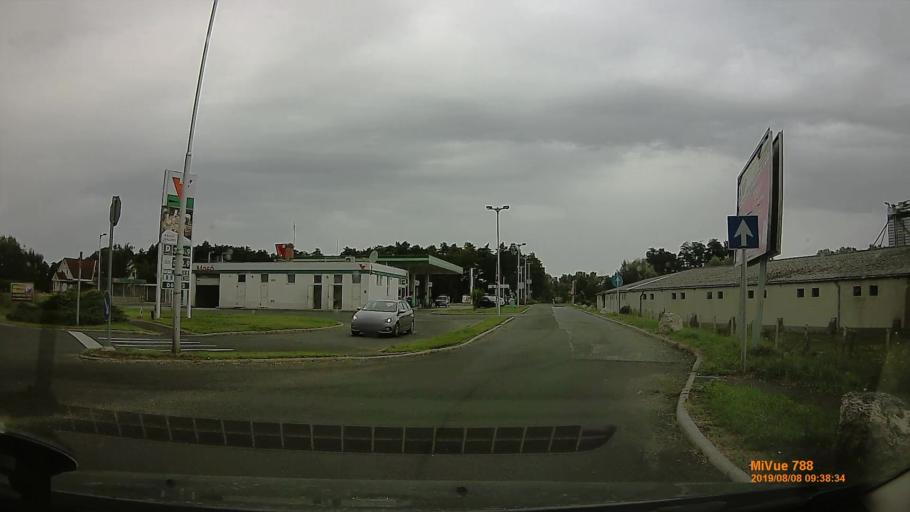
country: HU
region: Vas
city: Vasvar
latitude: 47.0539
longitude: 16.7909
